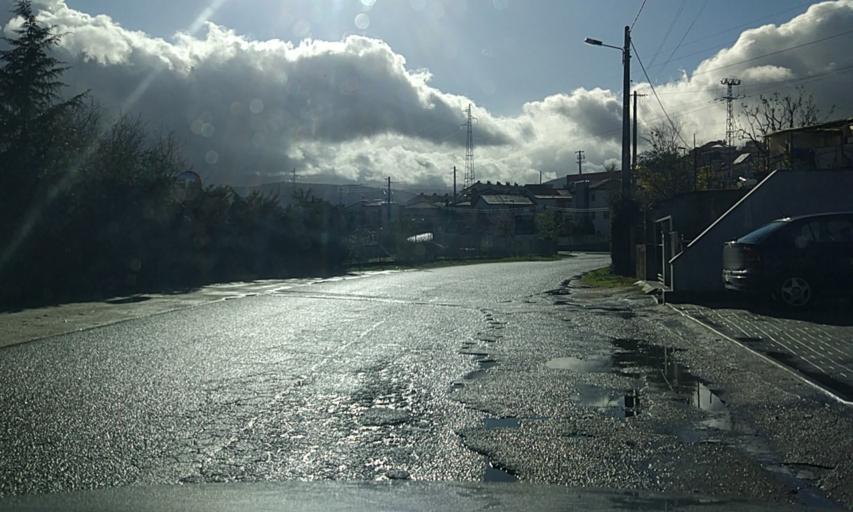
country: PT
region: Viseu
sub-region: Lamego
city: Lamego
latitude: 41.1056
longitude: -7.7937
